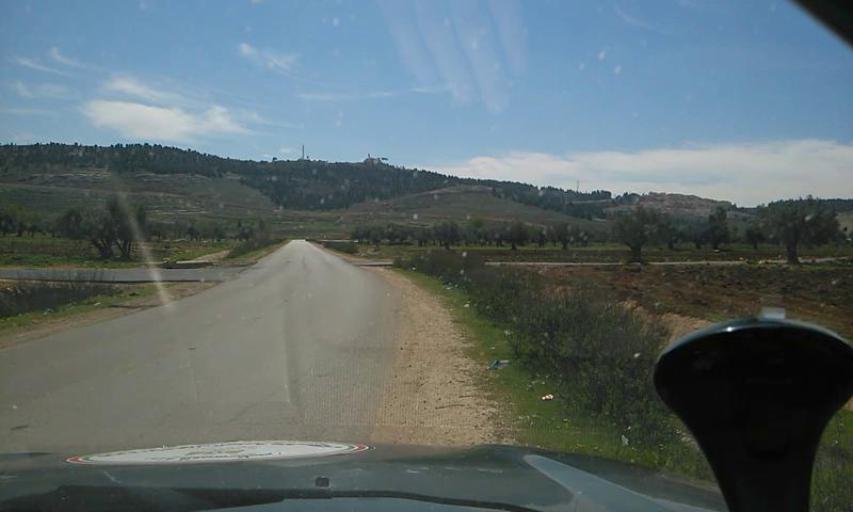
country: PS
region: West Bank
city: Al Jib
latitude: 31.8482
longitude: 35.1804
